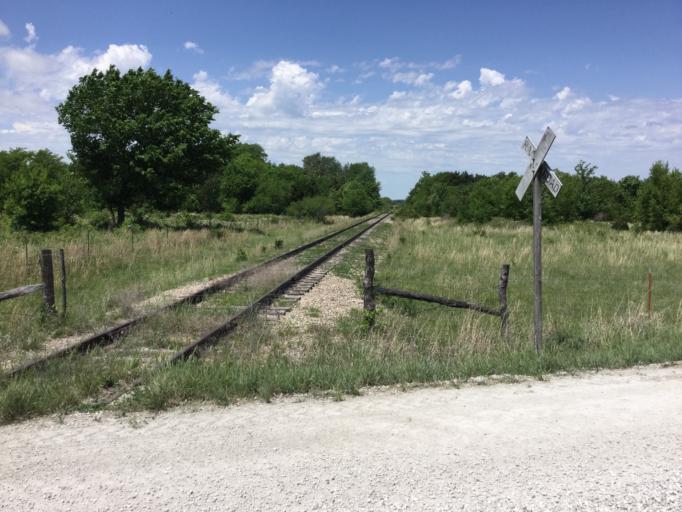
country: US
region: Kansas
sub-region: Coffey County
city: Burlington
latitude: 38.1703
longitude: -95.5362
